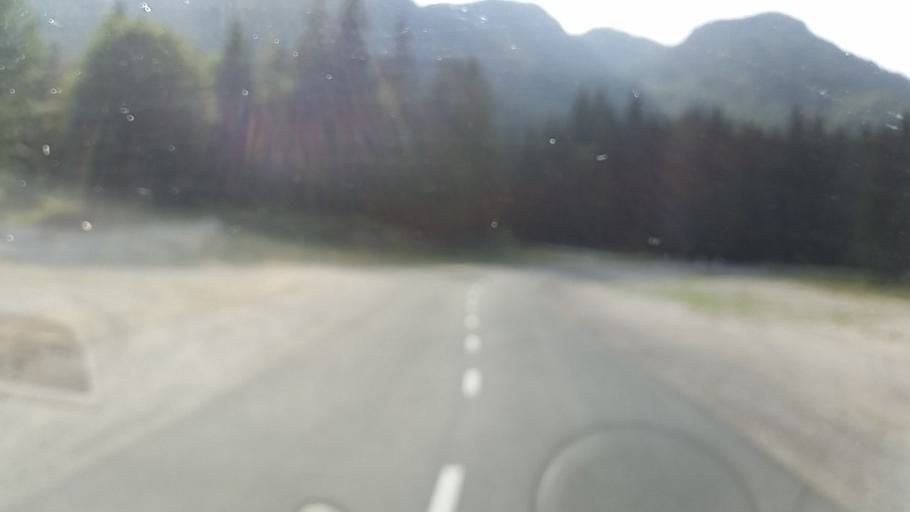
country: SI
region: Bohinj
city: Bohinjska Bistrica
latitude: 46.2416
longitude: 14.0094
